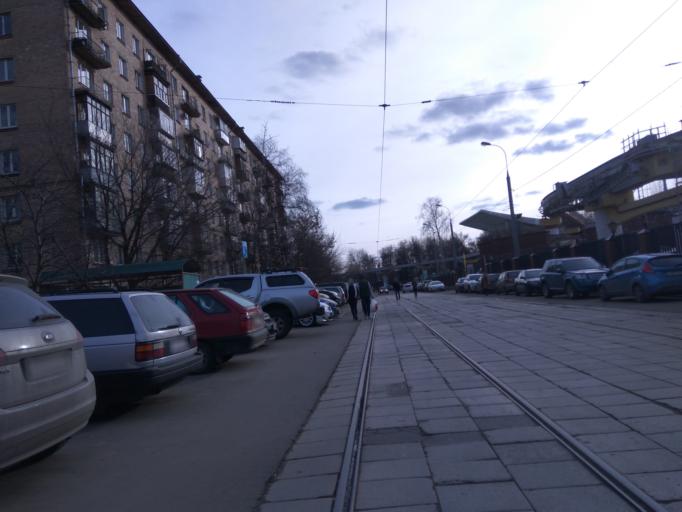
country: RU
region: Moscow
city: Leonovo
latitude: 55.8316
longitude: 37.6468
